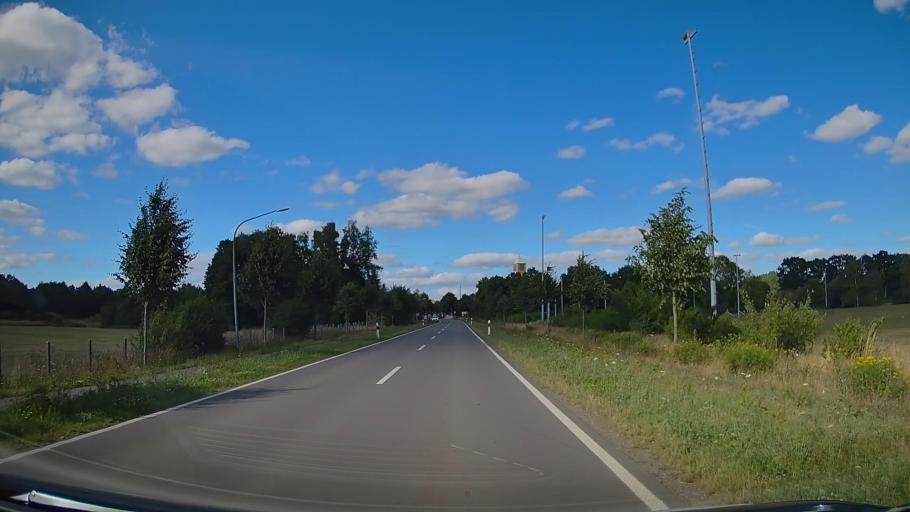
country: DE
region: Lower Saxony
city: Loningen
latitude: 52.7291
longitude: 7.7541
